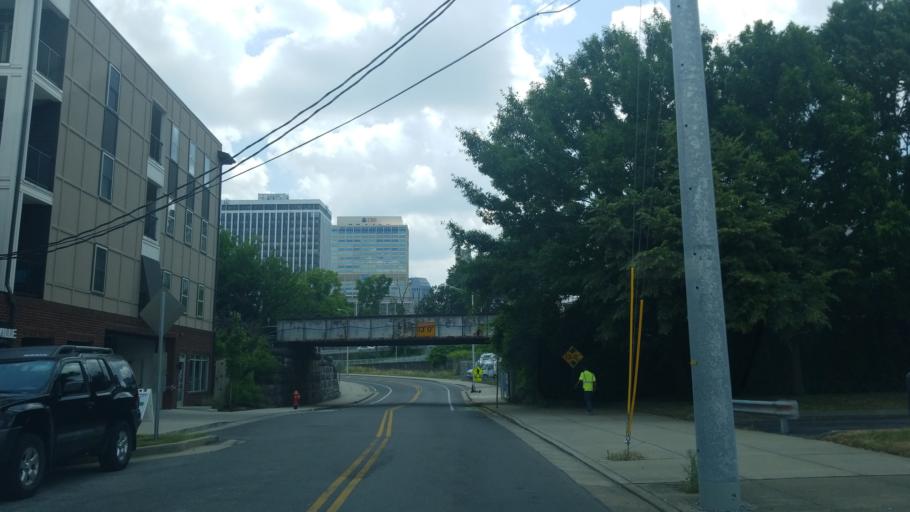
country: US
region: Tennessee
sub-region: Davidson County
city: Nashville
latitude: 36.1702
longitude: -86.7832
